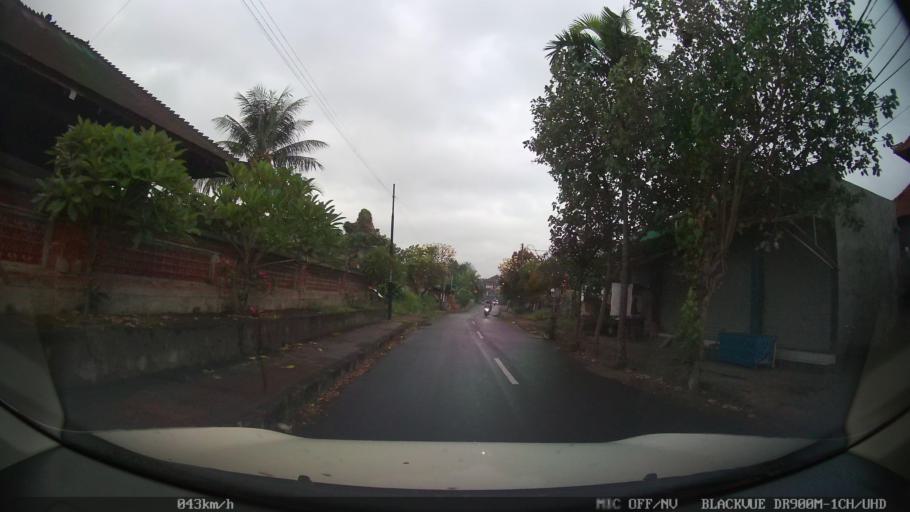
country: ID
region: Bali
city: Banjar Desa
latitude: -8.5841
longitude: 115.2785
